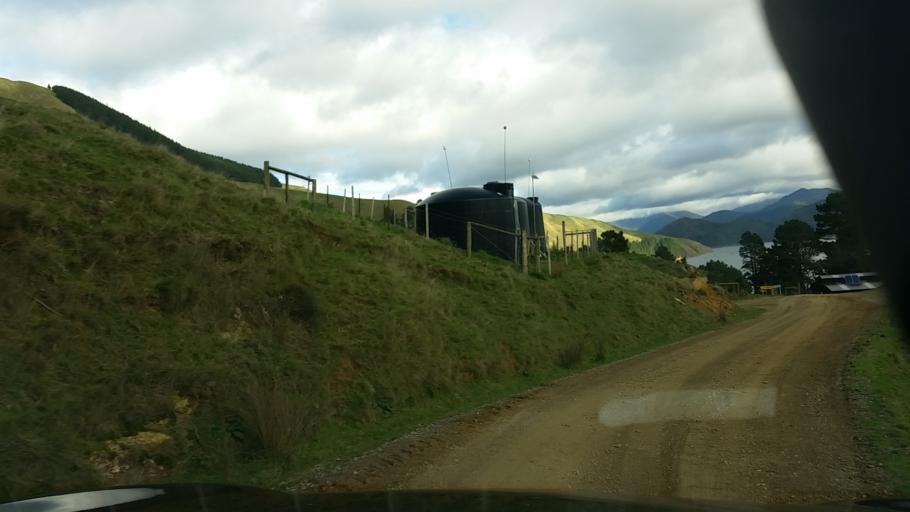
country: NZ
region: Marlborough
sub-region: Marlborough District
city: Picton
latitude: -40.9909
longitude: 173.8320
